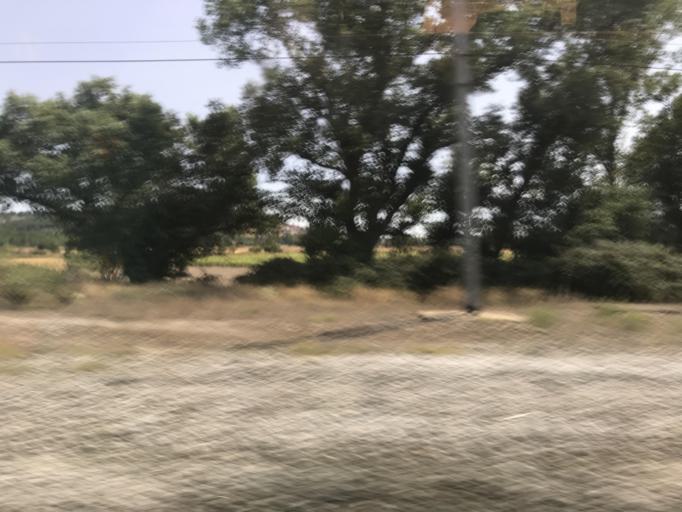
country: ES
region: Castille and Leon
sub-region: Provincia de Burgos
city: Villaquiran de los Infantes
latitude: 42.2140
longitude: -4.0014
